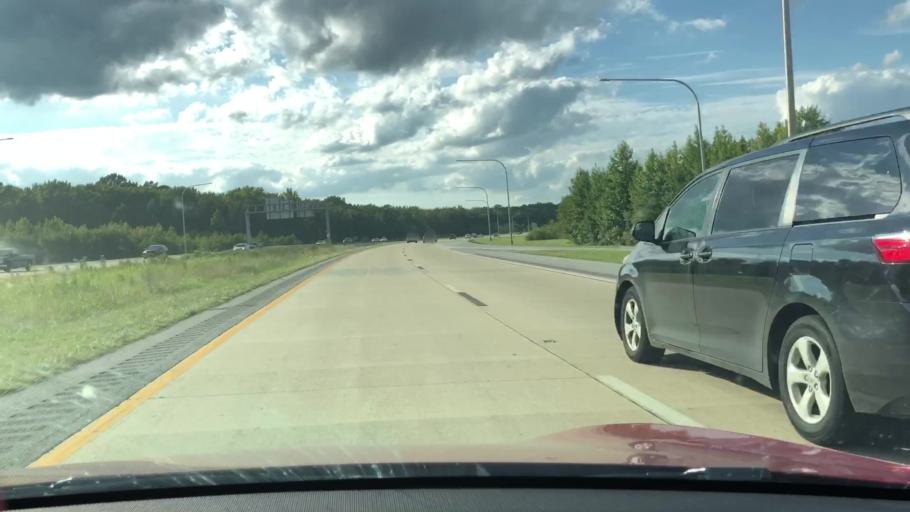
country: US
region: Delaware
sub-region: Kent County
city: Clayton
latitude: 39.3345
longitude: -75.6321
